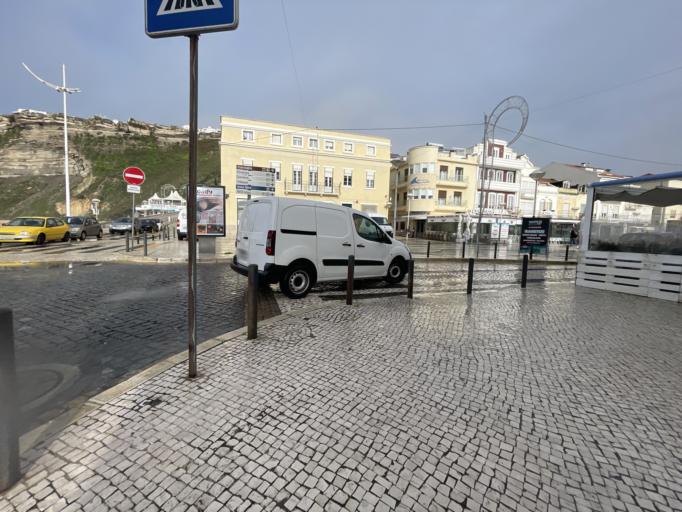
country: PT
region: Leiria
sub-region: Nazare
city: Nazare
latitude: 39.6016
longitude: -9.0738
